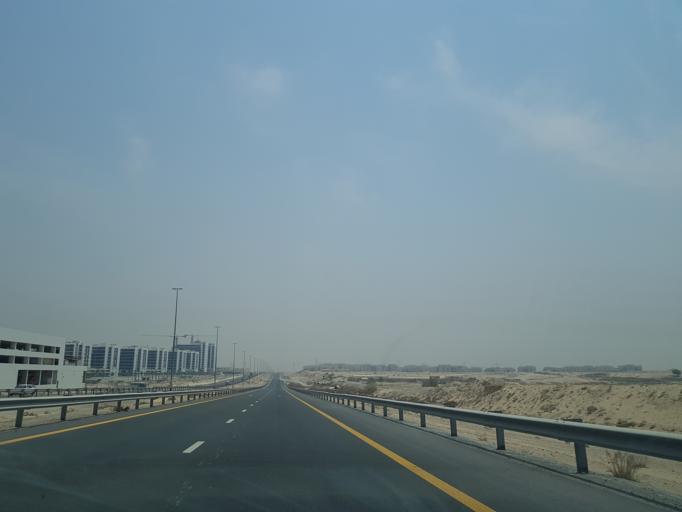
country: AE
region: Dubai
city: Dubai
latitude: 25.0191
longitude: 55.2442
